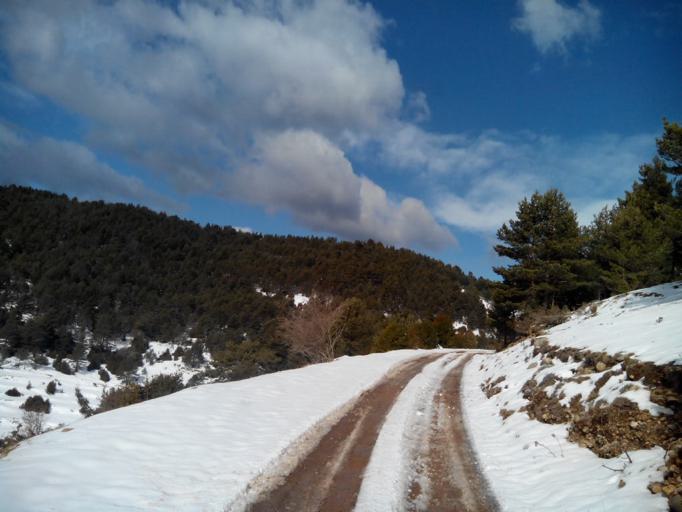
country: ES
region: Catalonia
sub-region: Provincia de Barcelona
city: Sant Julia de Cerdanyola
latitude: 42.1936
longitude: 1.9267
